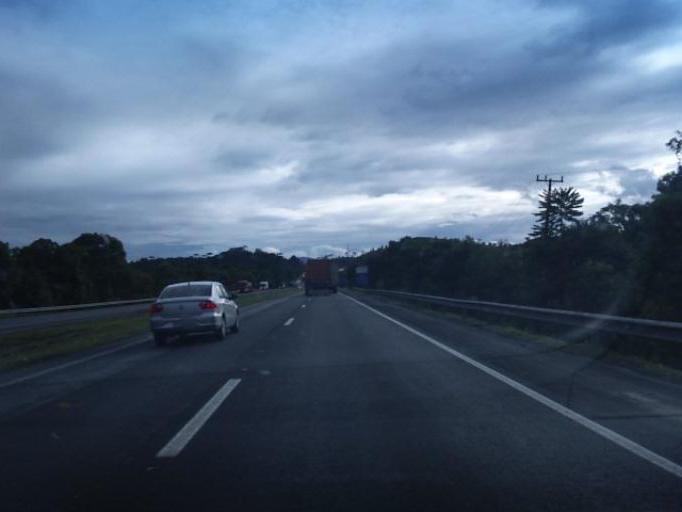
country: BR
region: Parana
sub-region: Campina Grande Do Sul
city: Campina Grande do Sul
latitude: -25.2813
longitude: -48.9276
